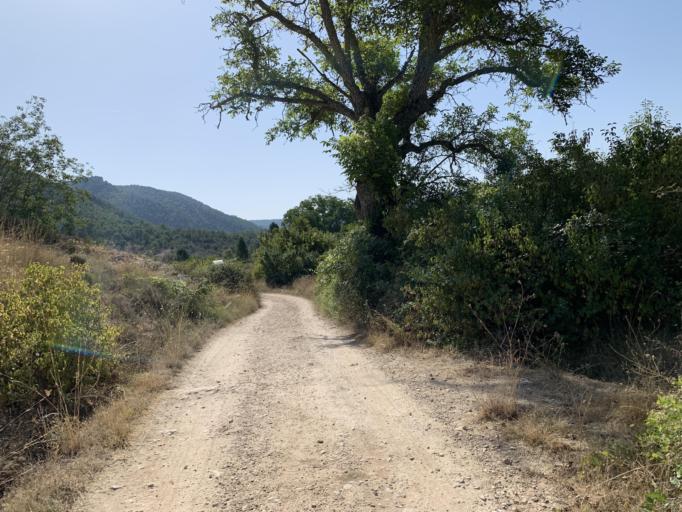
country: ES
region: Castille-La Mancha
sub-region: Provincia de Guadalajara
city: Ocentejo
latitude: 40.7666
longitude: -2.3957
